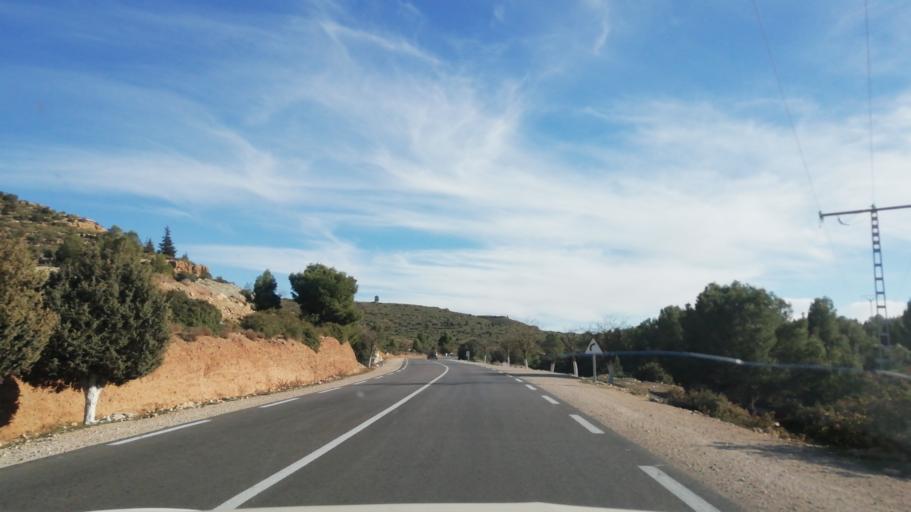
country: DZ
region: Tlemcen
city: Sebdou
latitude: 34.6031
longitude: -1.3257
